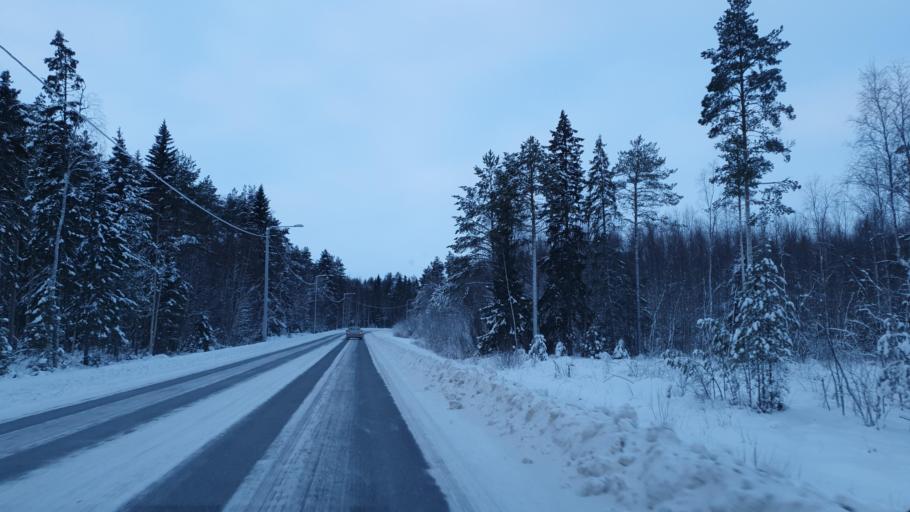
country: FI
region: Northern Ostrobothnia
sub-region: Oulu
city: Haukipudas
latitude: 65.1926
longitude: 25.3563
